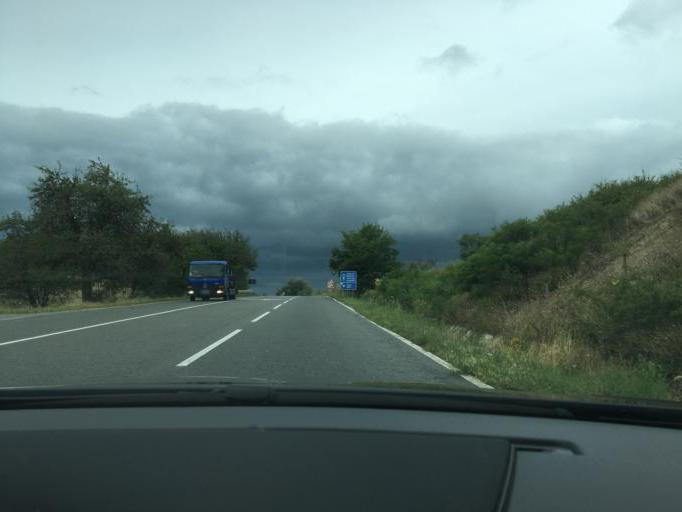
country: BG
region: Kyustendil
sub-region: Obshtina Bobovdol
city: Bobovdol
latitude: 42.2680
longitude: 22.9535
